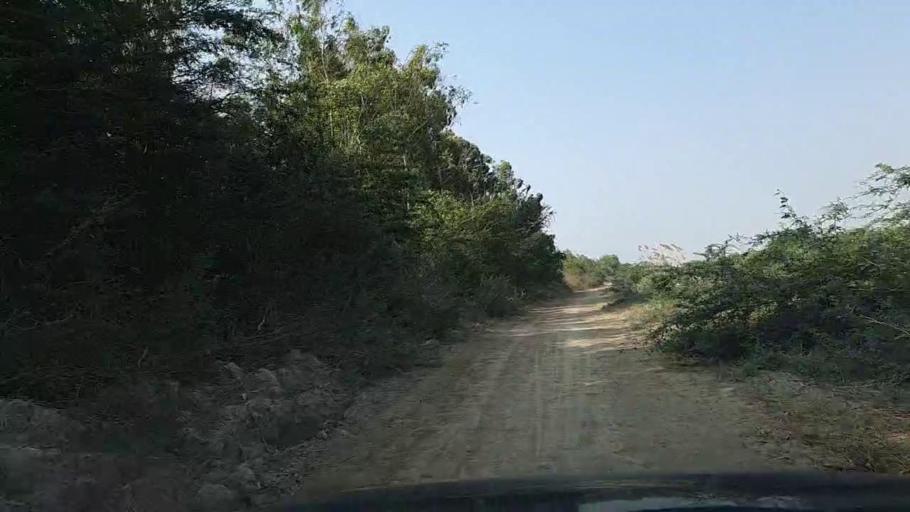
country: PK
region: Sindh
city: Gharo
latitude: 24.7284
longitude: 67.7134
